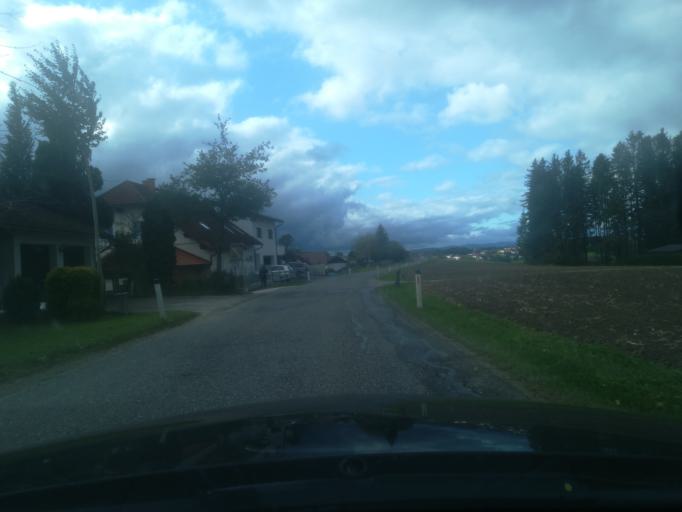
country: AT
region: Upper Austria
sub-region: Politischer Bezirk Urfahr-Umgebung
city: Herzogsdorf
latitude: 48.4228
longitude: 14.1502
